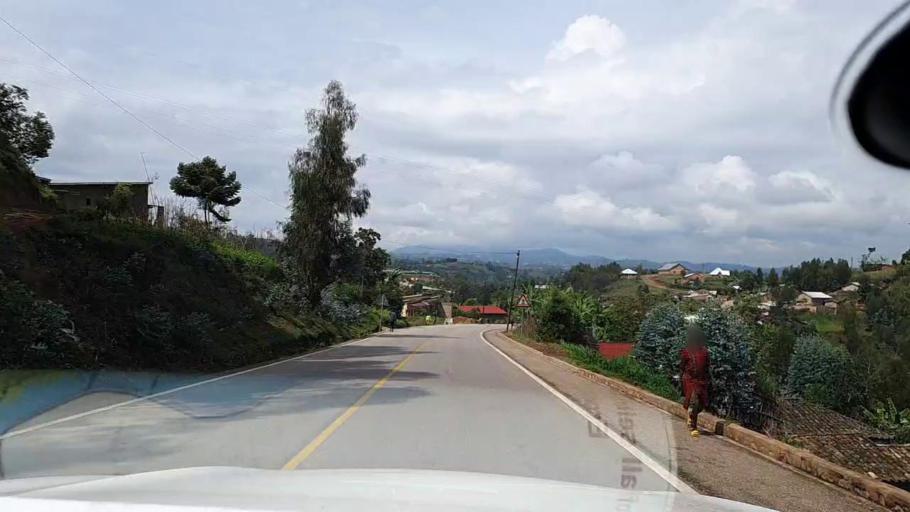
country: RW
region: Southern Province
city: Nzega
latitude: -2.4849
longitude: 29.5182
